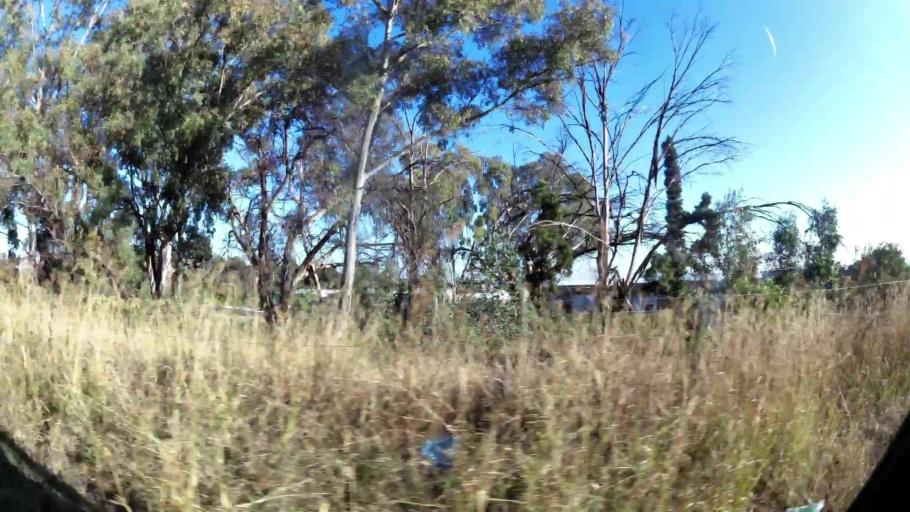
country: ZA
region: Gauteng
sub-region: City of Johannesburg Metropolitan Municipality
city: Midrand
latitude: -26.0279
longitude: 28.0401
